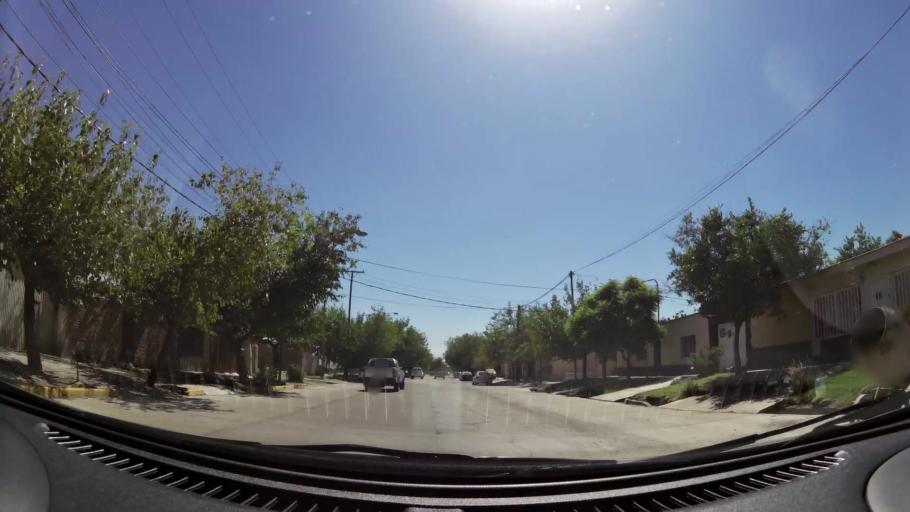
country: AR
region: Mendoza
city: Mendoza
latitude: -32.8937
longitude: -68.8174
